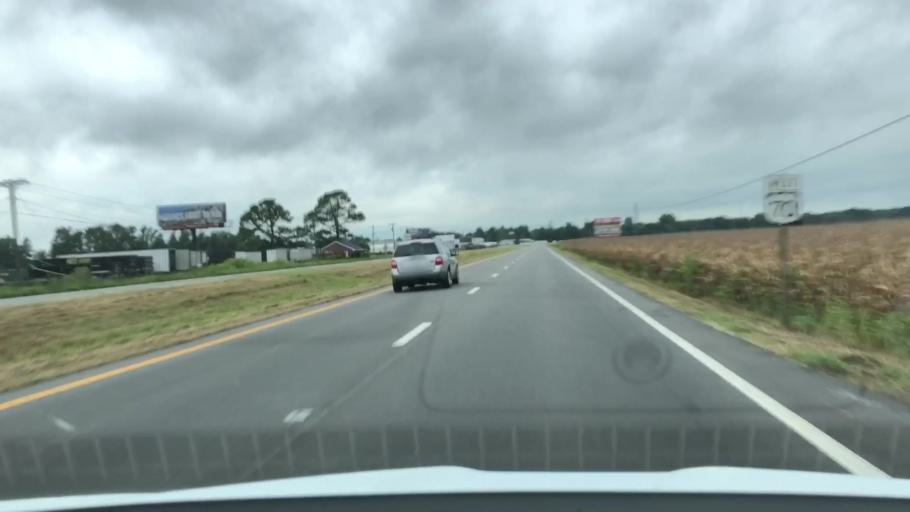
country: US
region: North Carolina
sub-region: Lenoir County
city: La Grange
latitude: 35.2673
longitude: -77.7322
